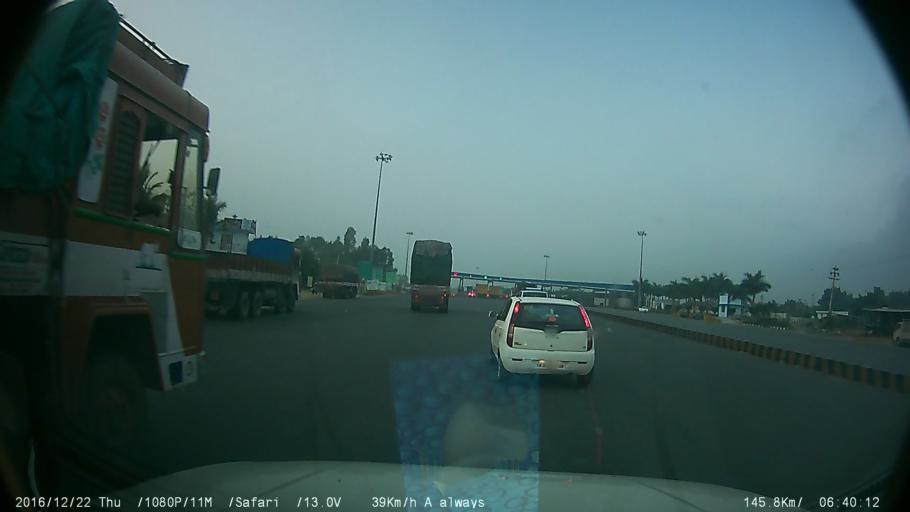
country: IN
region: Tamil Nadu
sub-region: Dharmapuri
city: Dharmapuri
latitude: 12.0079
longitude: 78.0819
